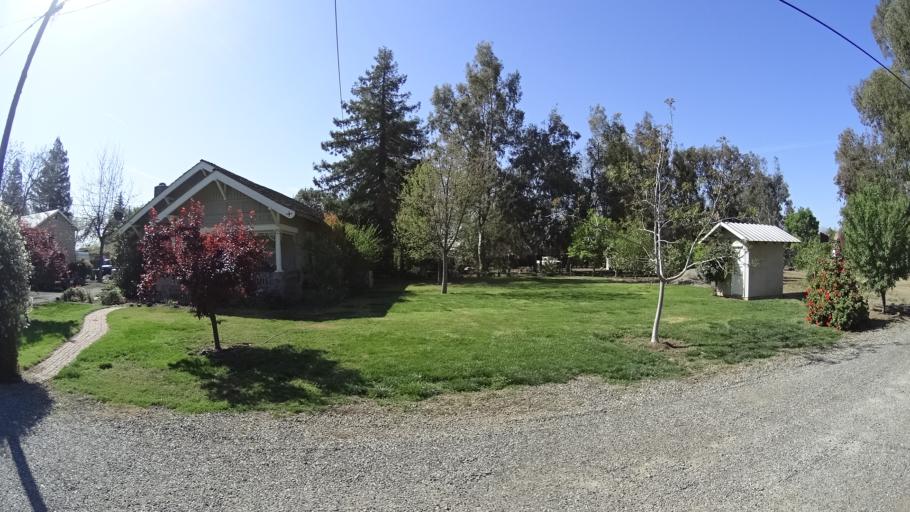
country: US
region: California
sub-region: Glenn County
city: Willows
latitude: 39.5334
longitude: -122.1964
